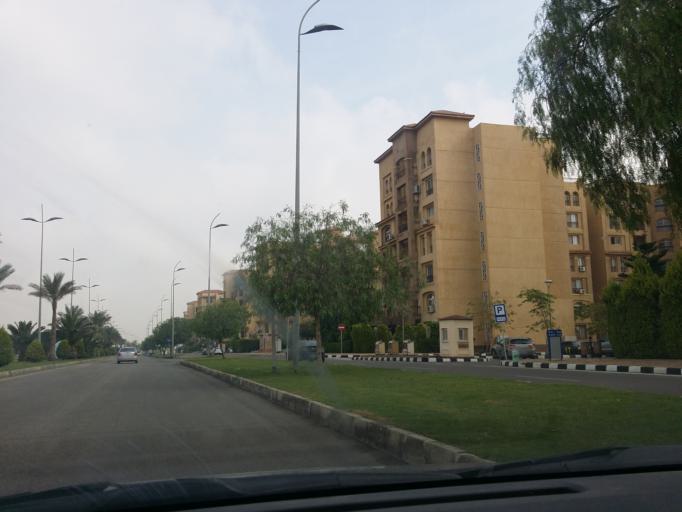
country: EG
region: Muhafazat al Qalyubiyah
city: Al Khankah
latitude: 30.1009
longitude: 31.6334
